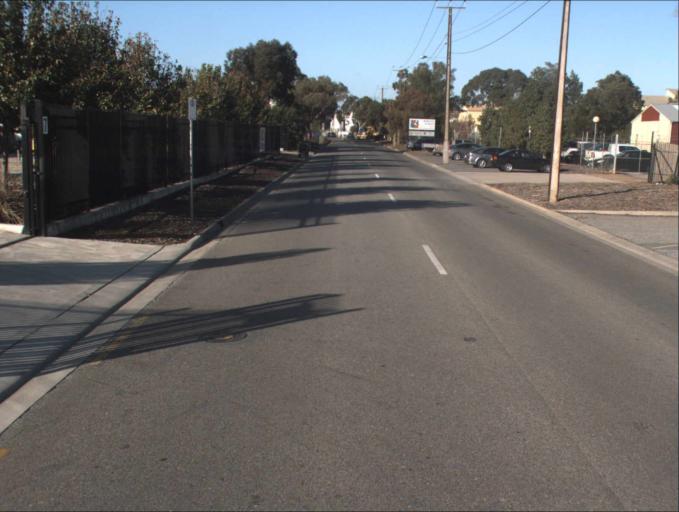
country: AU
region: South Australia
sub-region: Port Adelaide Enfield
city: Blair Athol
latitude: -34.8498
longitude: 138.5851
